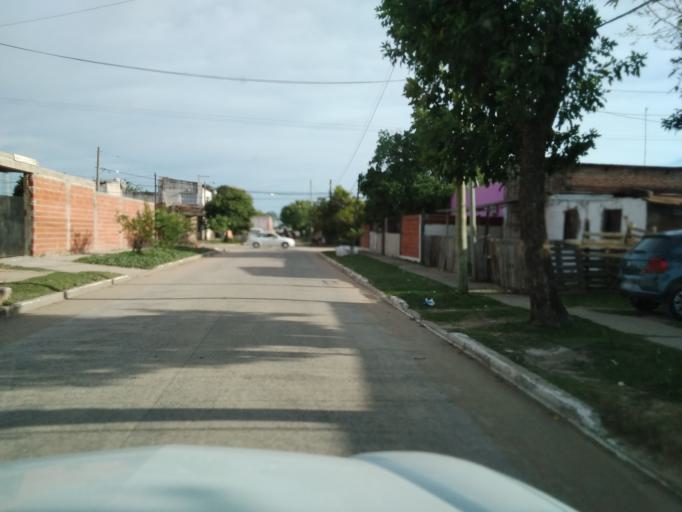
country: AR
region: Corrientes
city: Corrientes
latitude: -27.4914
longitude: -58.8438
